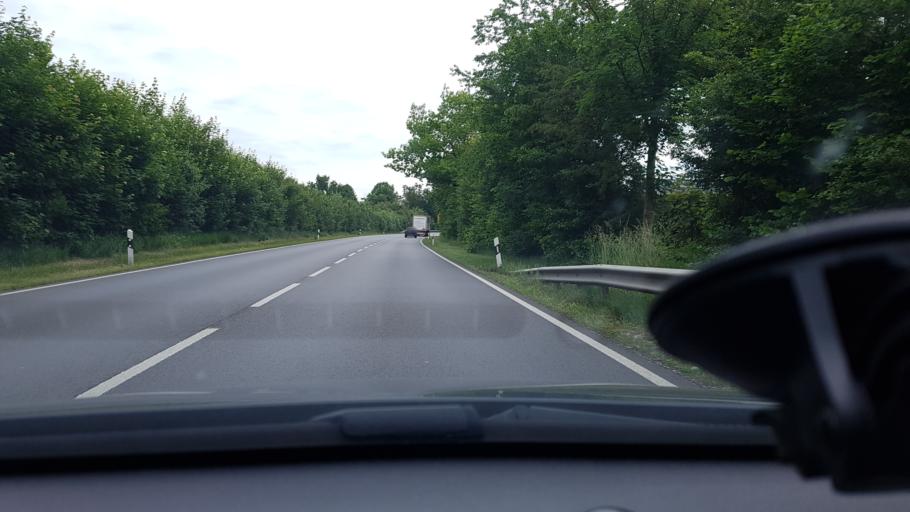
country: DE
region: Bavaria
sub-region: Lower Bavaria
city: Pocking
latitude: 48.3935
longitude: 13.3052
